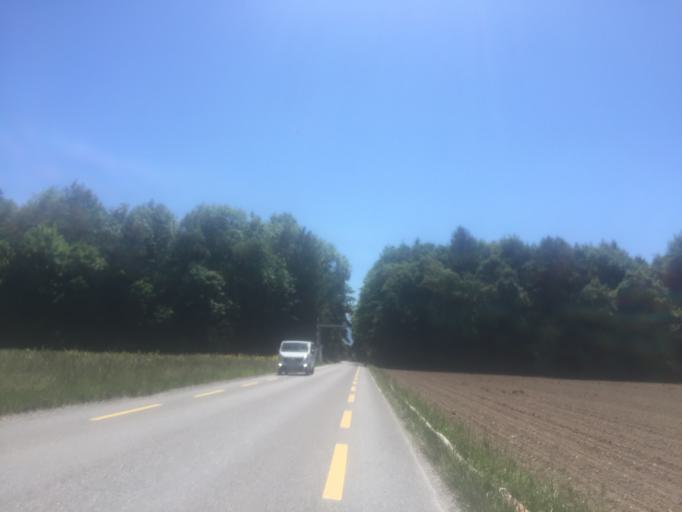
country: CH
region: Bern
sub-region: Thun District
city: Thierachern
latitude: 46.7473
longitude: 7.5917
